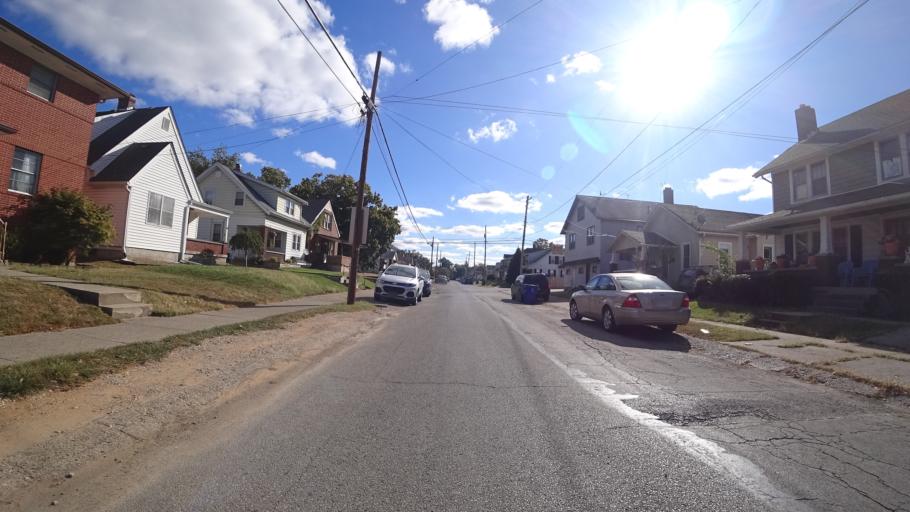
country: US
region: Ohio
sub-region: Butler County
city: Fairfield
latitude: 39.3662
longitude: -84.5565
